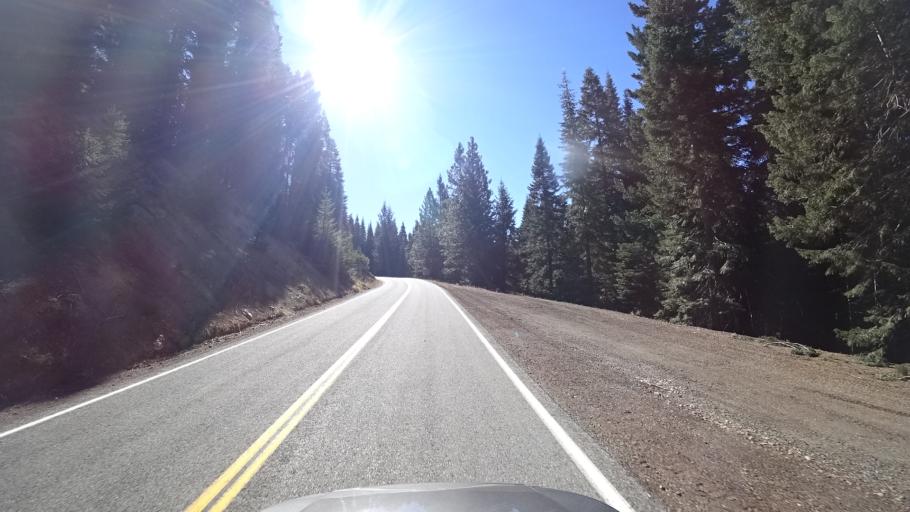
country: US
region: California
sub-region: Trinity County
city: Weaverville
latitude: 41.2290
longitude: -122.9303
